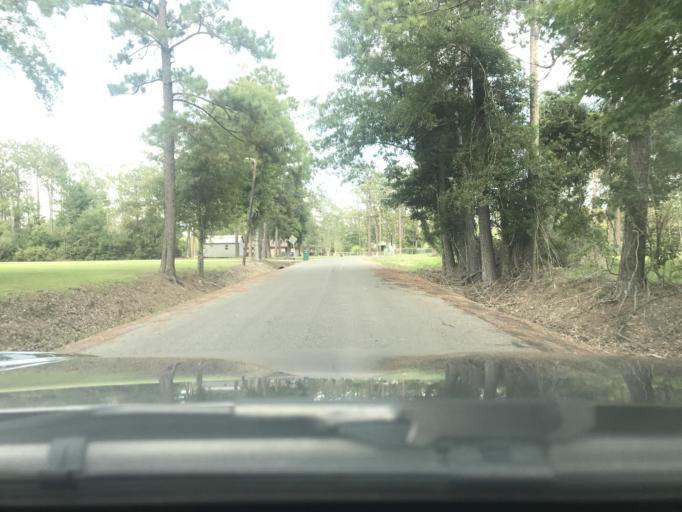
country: US
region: Louisiana
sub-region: Calcasieu Parish
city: Moss Bluff
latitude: 30.3390
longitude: -93.2635
